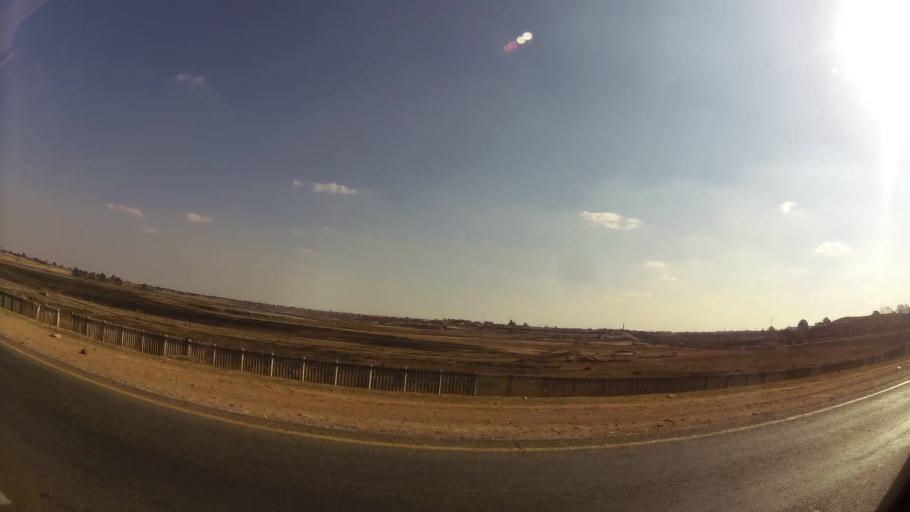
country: ZA
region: Gauteng
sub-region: Ekurhuleni Metropolitan Municipality
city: Benoni
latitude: -26.2245
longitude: 28.3201
